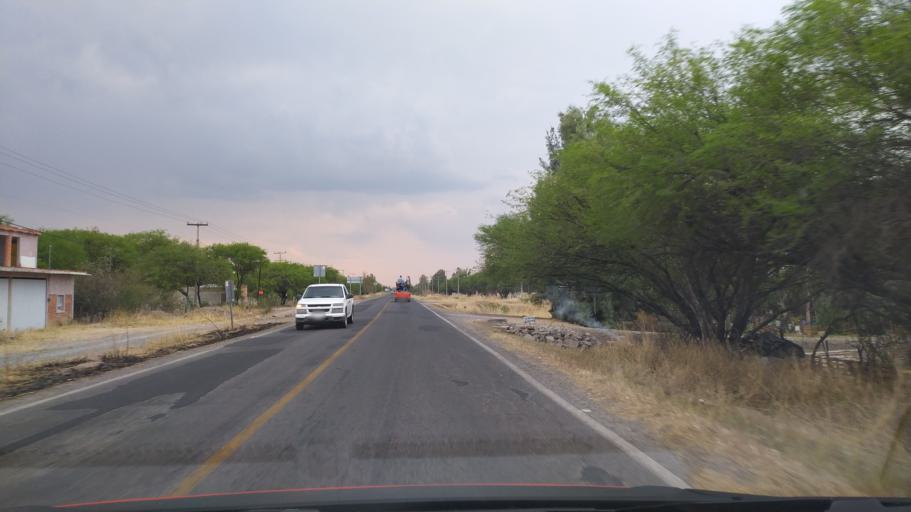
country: MX
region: Guanajuato
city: Ciudad Manuel Doblado
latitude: 20.7931
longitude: -101.9063
